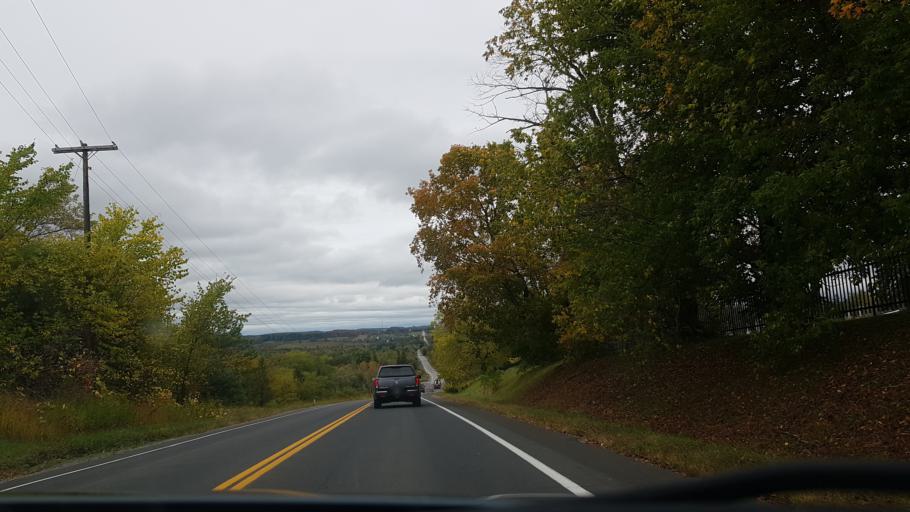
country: CA
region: Ontario
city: Omemee
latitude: 44.2152
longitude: -78.4754
